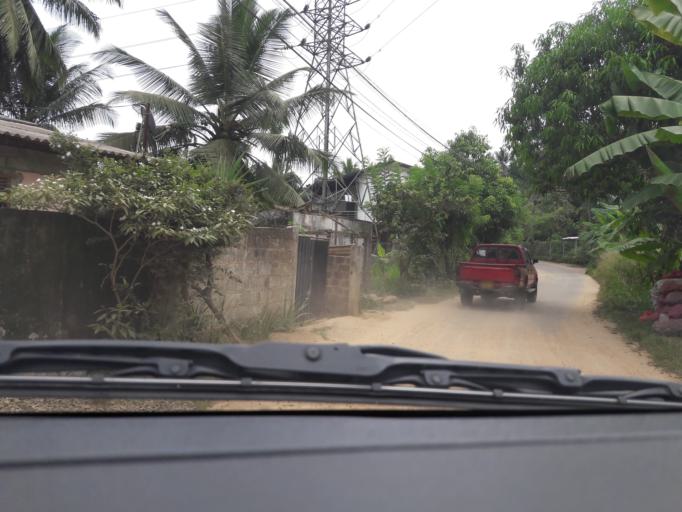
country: LK
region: Southern
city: Unawatuna
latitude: 6.0533
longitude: 80.2489
